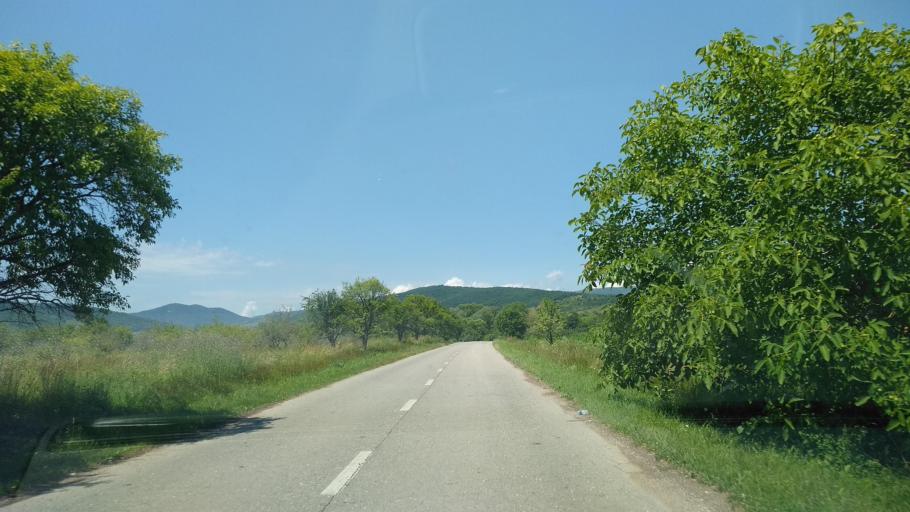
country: RO
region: Hunedoara
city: Densus
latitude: 45.5787
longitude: 22.8228
